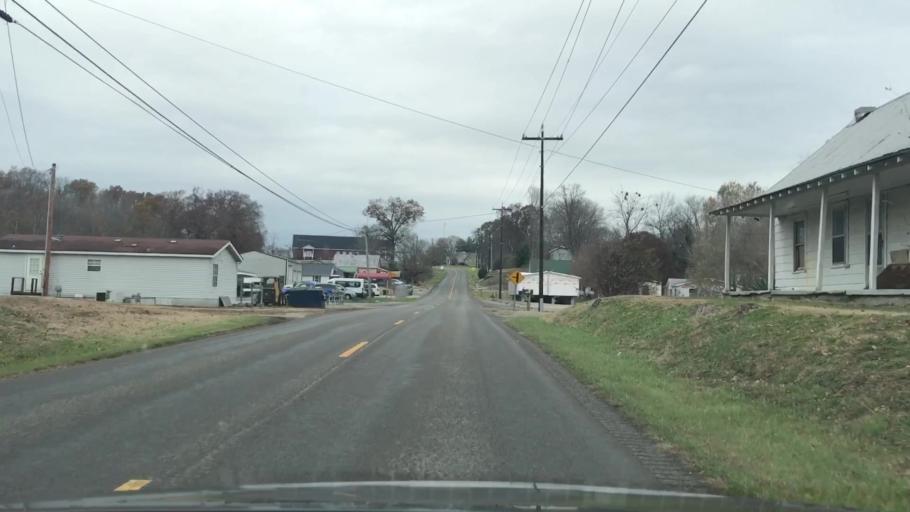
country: US
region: Kentucky
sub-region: Metcalfe County
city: Edmonton
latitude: 36.9680
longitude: -85.6092
